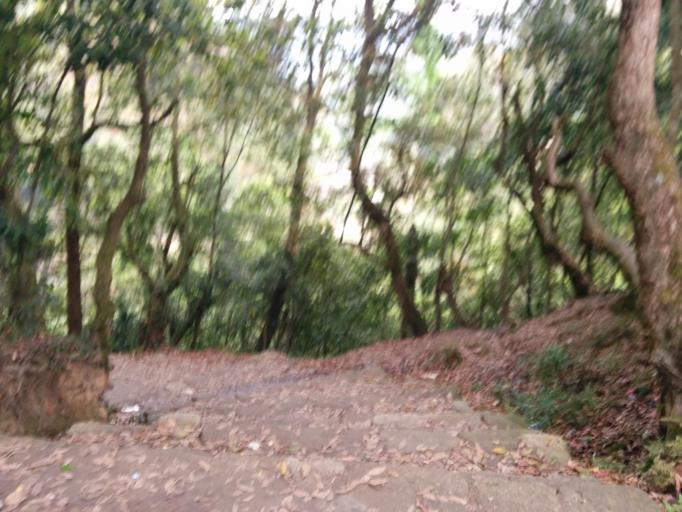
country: NP
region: Central Region
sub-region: Bagmati Zone
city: Bhaktapur
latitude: 27.7713
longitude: 85.4263
